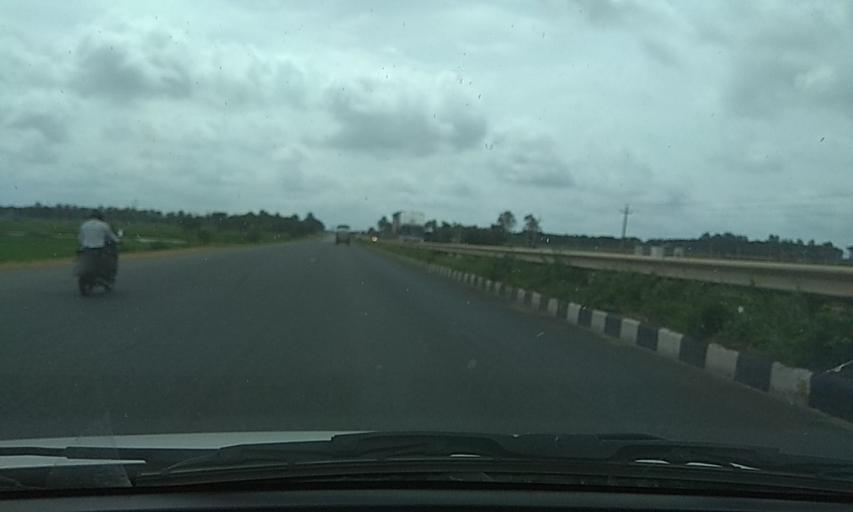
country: IN
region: Karnataka
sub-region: Davanagere
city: Harihar
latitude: 14.4493
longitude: 75.8809
